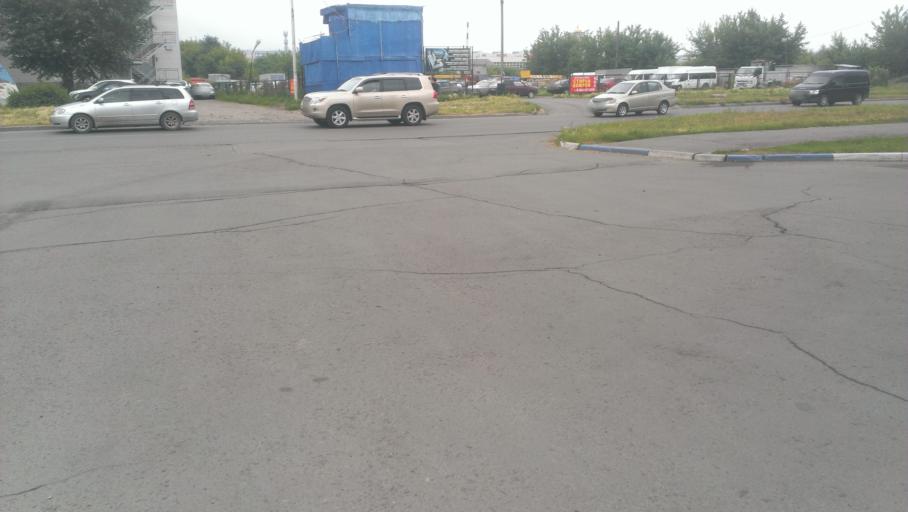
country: RU
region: Altai Krai
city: Novosilikatnyy
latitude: 53.3385
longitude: 83.6785
